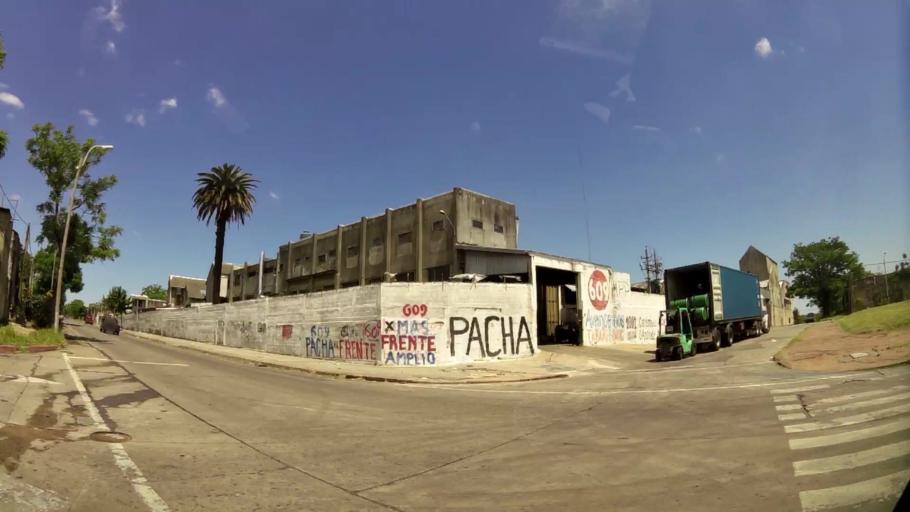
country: UY
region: Montevideo
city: Montevideo
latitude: -34.8535
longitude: -56.2367
